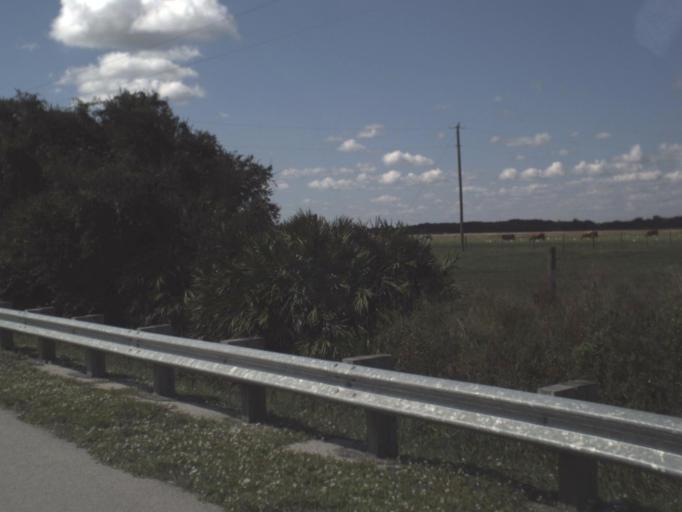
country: US
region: Florida
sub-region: Hendry County
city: Port LaBelle
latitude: 26.8124
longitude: -81.3733
